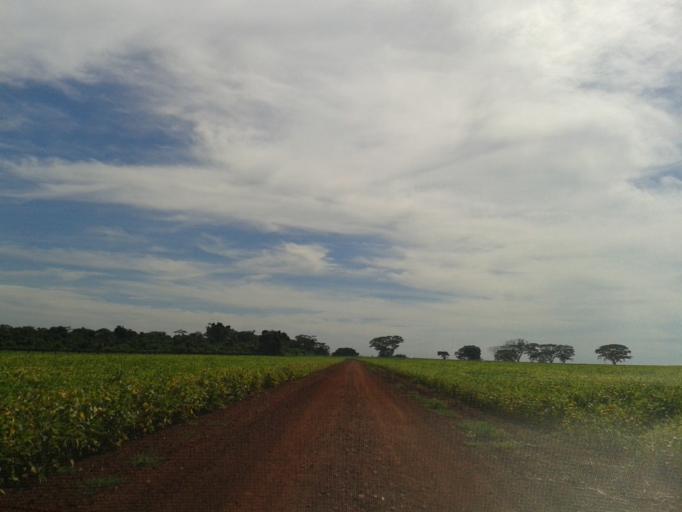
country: BR
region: Minas Gerais
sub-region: Capinopolis
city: Capinopolis
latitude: -18.6384
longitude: -49.7233
